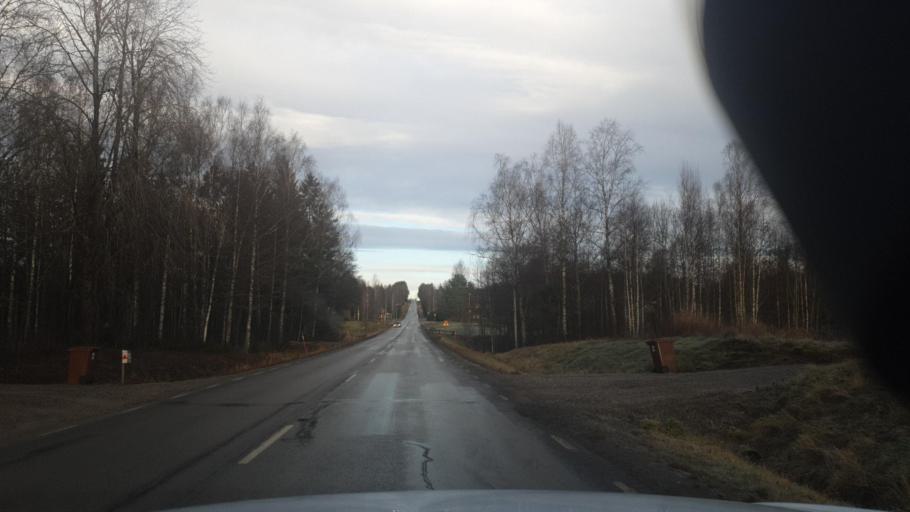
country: SE
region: Vaermland
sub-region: Arvika Kommun
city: Arvika
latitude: 59.6808
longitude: 12.6310
